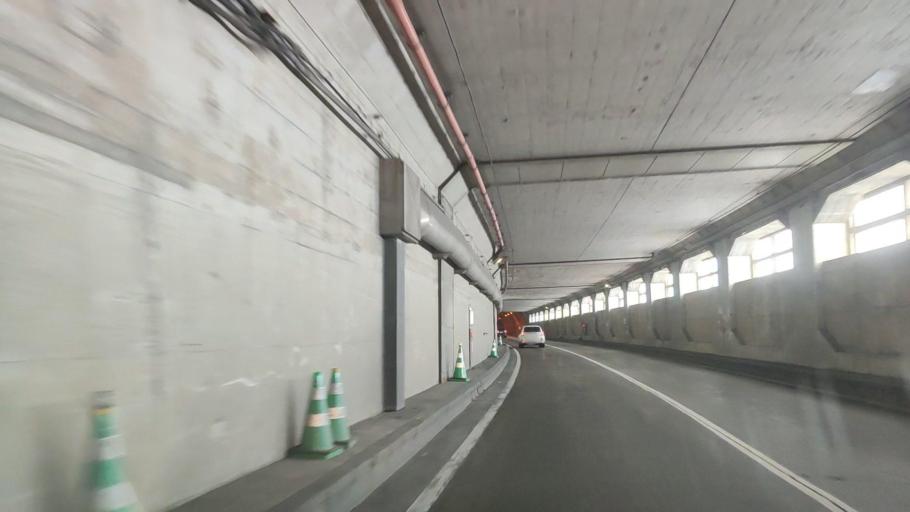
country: JP
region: Hokkaido
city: Rumoi
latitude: 43.7981
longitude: 141.3779
